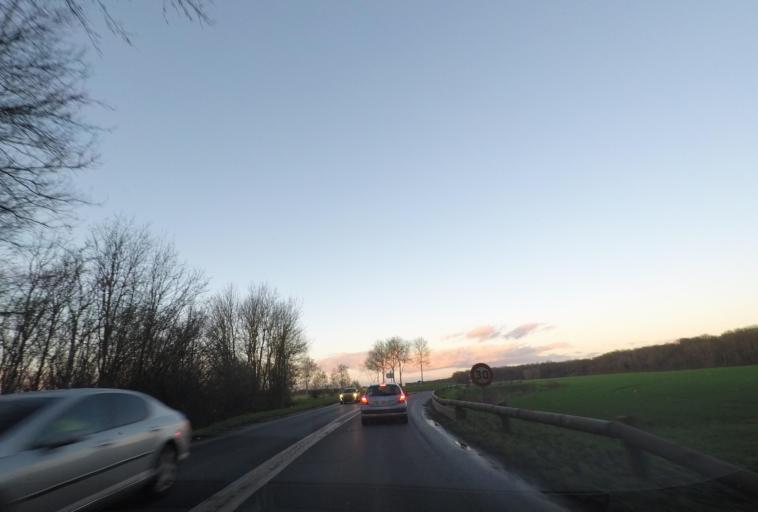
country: FR
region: Ile-de-France
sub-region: Departement de l'Essonne
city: Vert-le-Grand
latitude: 48.5841
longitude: 2.3672
